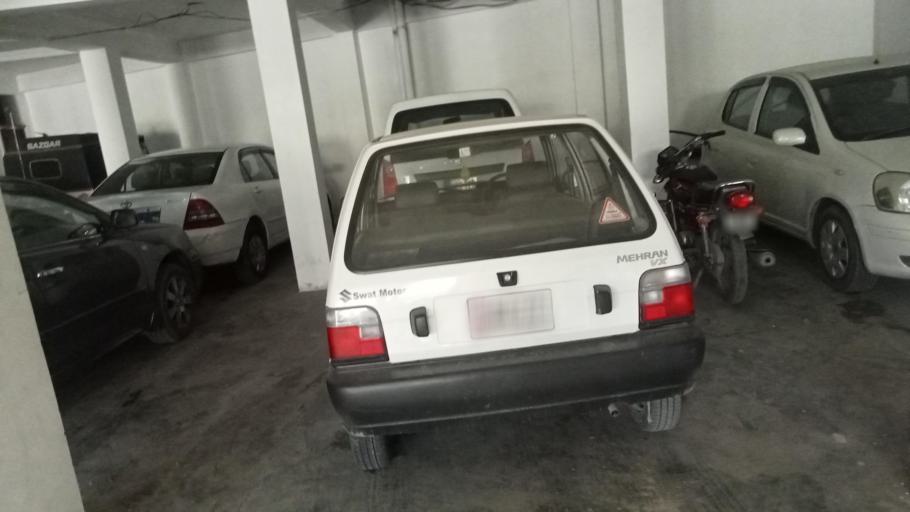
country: PK
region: Khyber Pakhtunkhwa
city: Mingora
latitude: 34.7678
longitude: 72.3602
